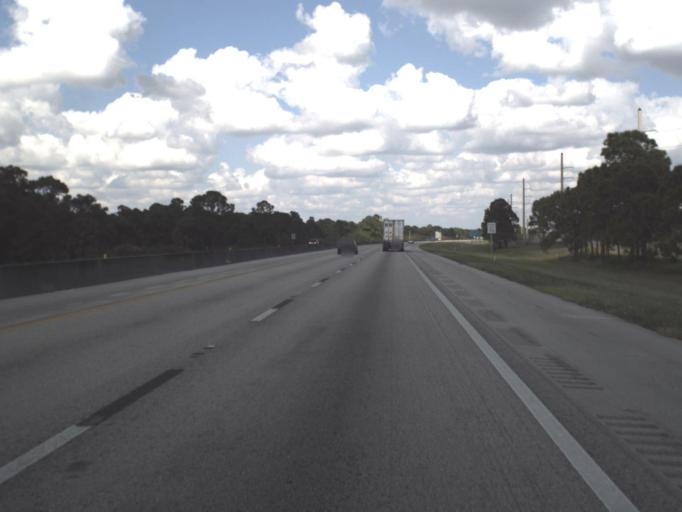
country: US
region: Florida
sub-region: Martin County
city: North River Shores
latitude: 27.2215
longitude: -80.3393
